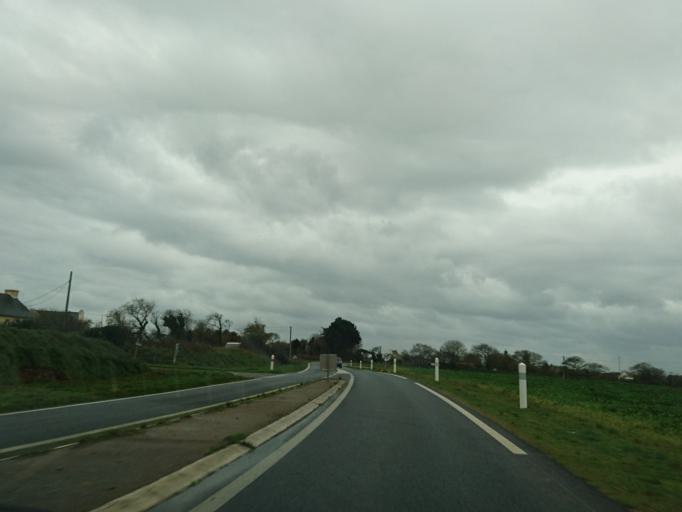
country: FR
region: Brittany
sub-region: Departement du Finistere
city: Plouzane
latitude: 48.3614
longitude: -4.6204
